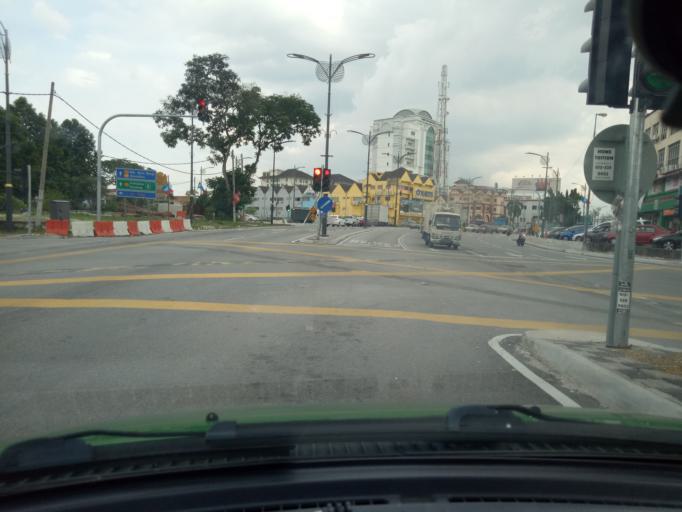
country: MY
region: Selangor
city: Kampong Baharu Balakong
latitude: 2.9971
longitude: 101.7872
